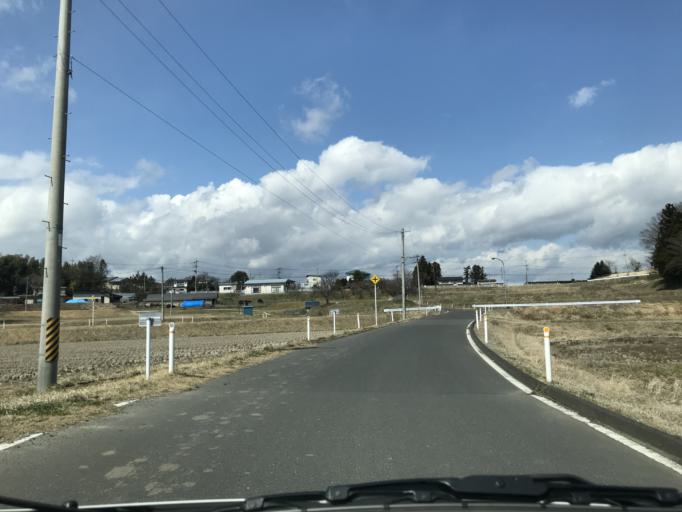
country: JP
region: Miyagi
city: Wakuya
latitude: 38.6762
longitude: 141.1193
